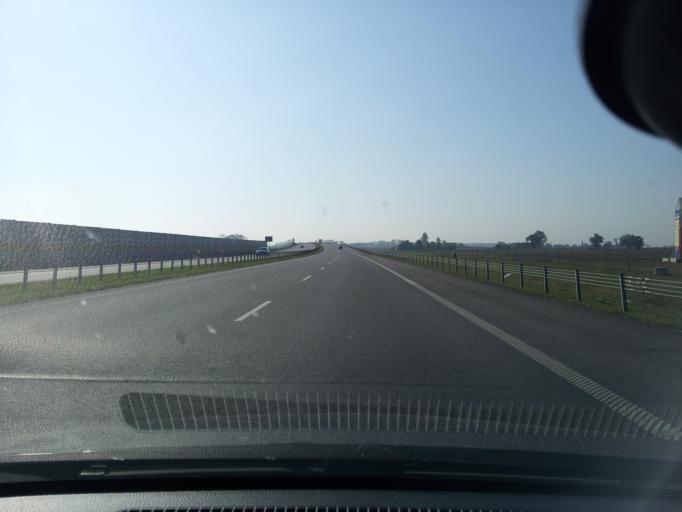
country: PL
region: Kujawsko-Pomorskie
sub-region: Powiat torunski
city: Lubicz Dolny
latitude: 53.1363
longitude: 18.7399
